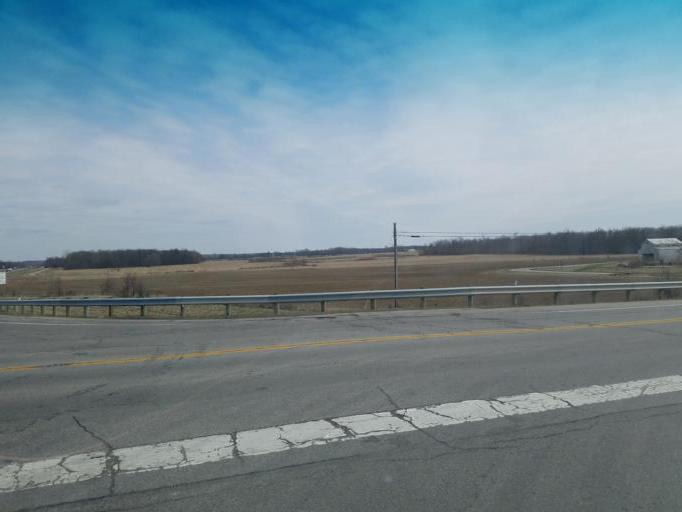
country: US
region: Ohio
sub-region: Crawford County
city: Crestline
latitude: 40.7610
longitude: -82.7465
